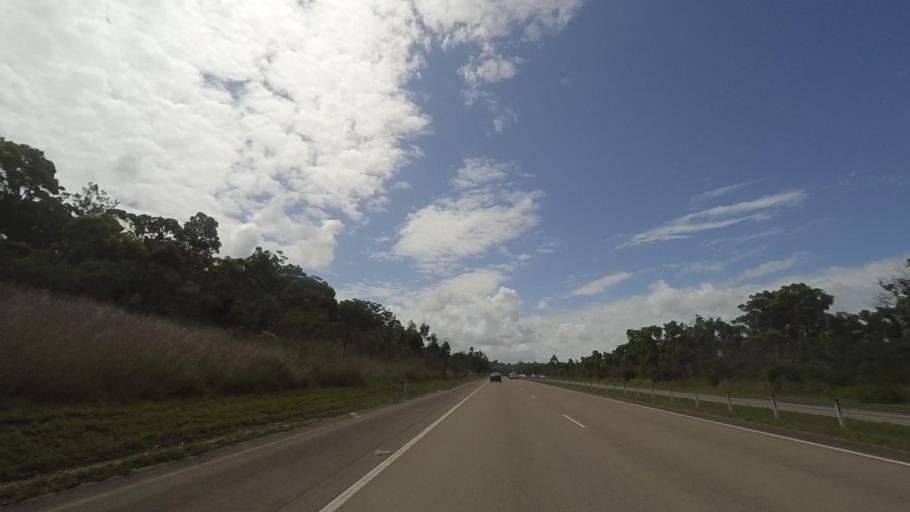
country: AU
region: New South Wales
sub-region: Lake Macquarie Shire
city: Windale
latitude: -32.9868
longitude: 151.6851
